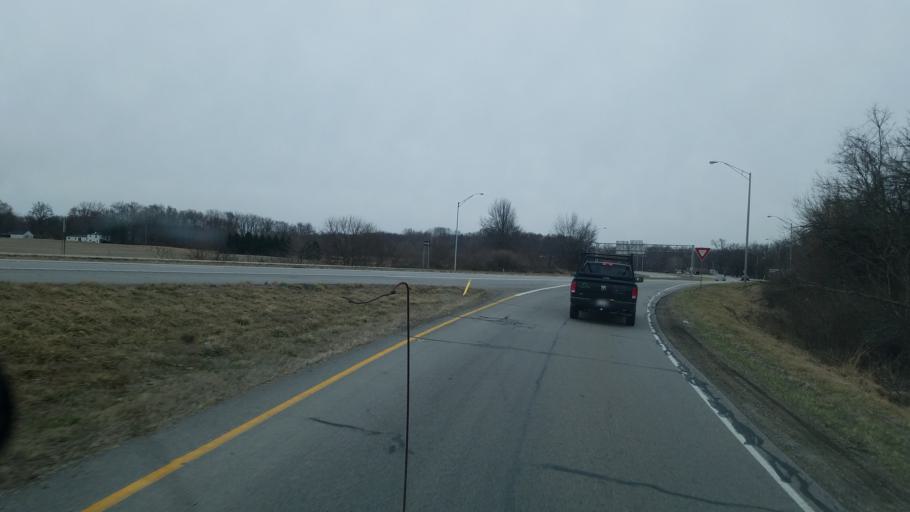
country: US
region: Indiana
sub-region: Marshall County
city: Plymouth
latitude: 41.3469
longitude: -86.2755
